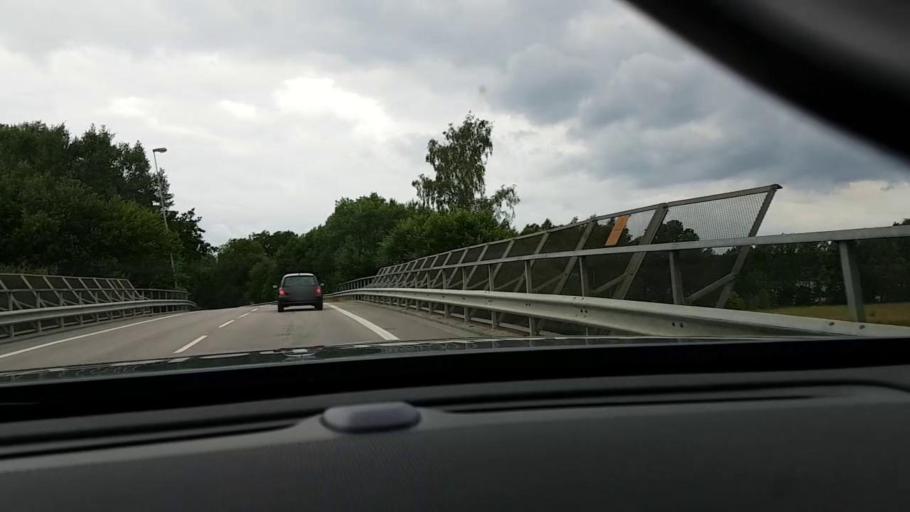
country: SE
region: Skane
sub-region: Hassleholms Kommun
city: Hassleholm
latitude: 56.1722
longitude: 13.7718
